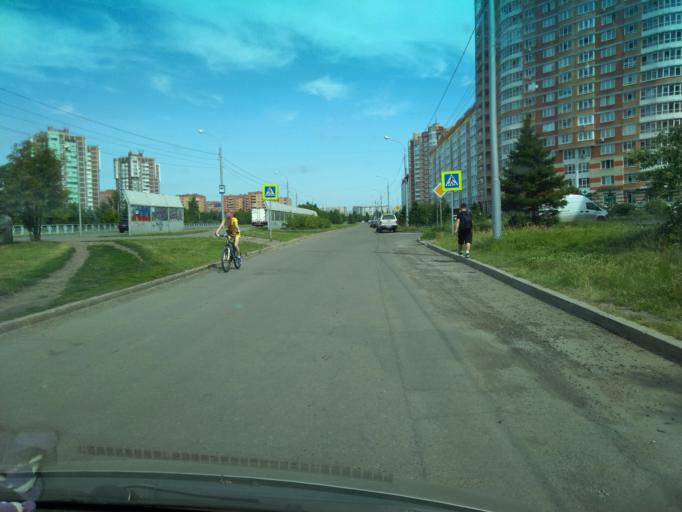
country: RU
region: Krasnoyarskiy
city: Krasnoyarsk
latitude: 56.0518
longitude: 92.9144
